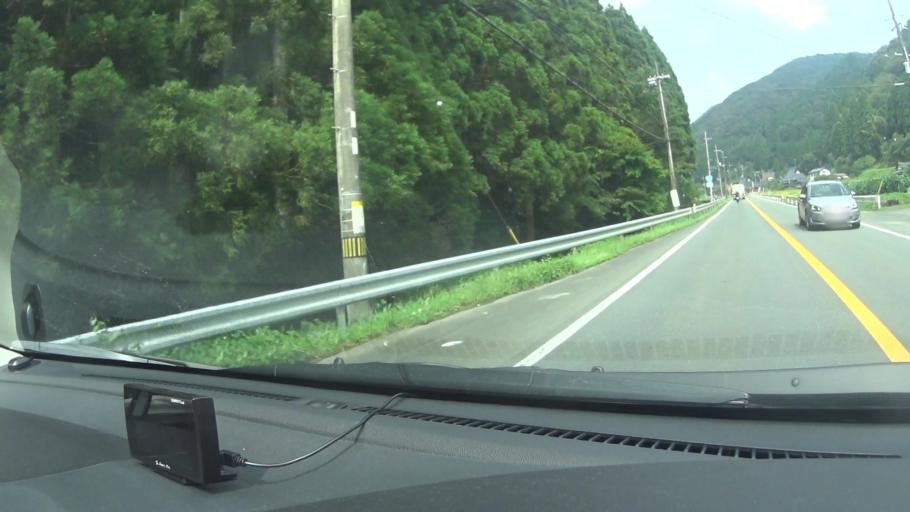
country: JP
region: Kyoto
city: Ayabe
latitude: 35.2303
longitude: 135.3343
